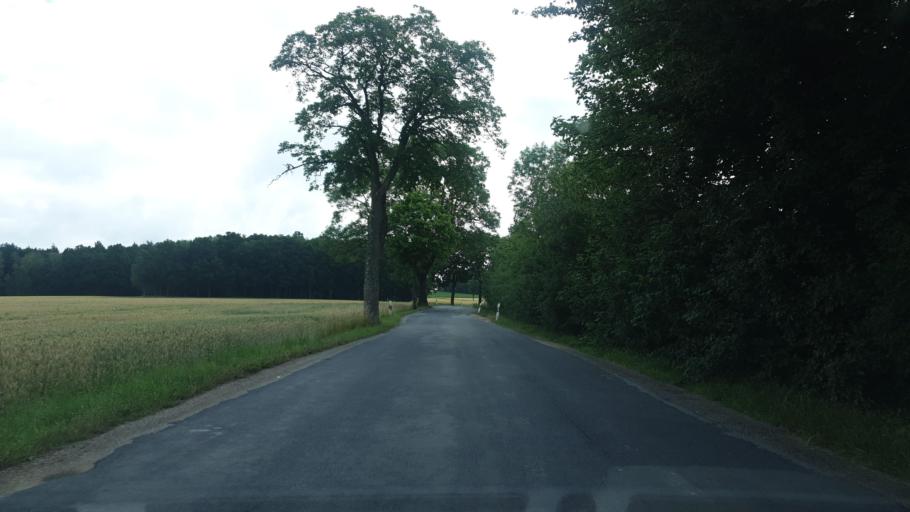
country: DE
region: Saxony
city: Limbach
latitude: 50.5895
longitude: 12.2361
